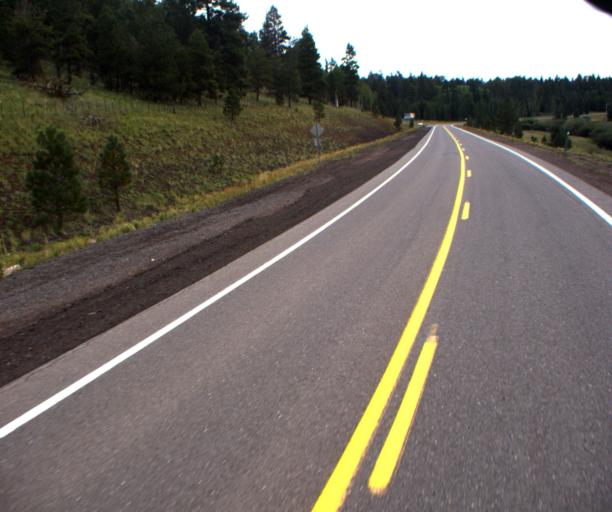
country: US
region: Arizona
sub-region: Apache County
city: Eagar
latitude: 34.0051
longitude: -109.5650
